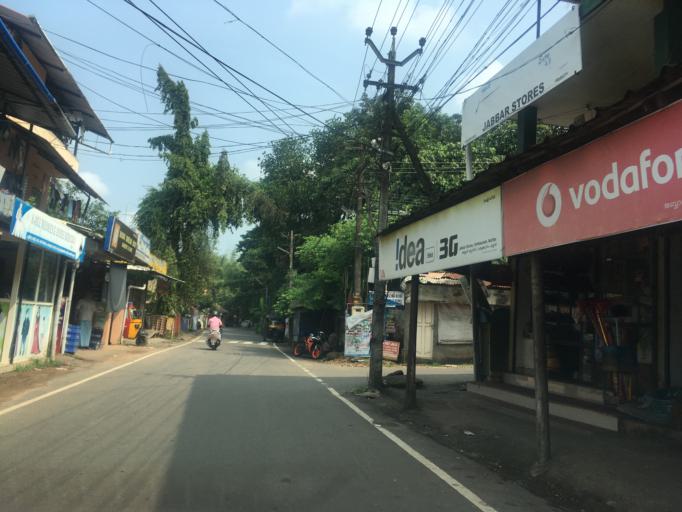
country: IN
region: Kerala
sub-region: Ernakulam
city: Elur
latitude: 10.0433
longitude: 76.3056
